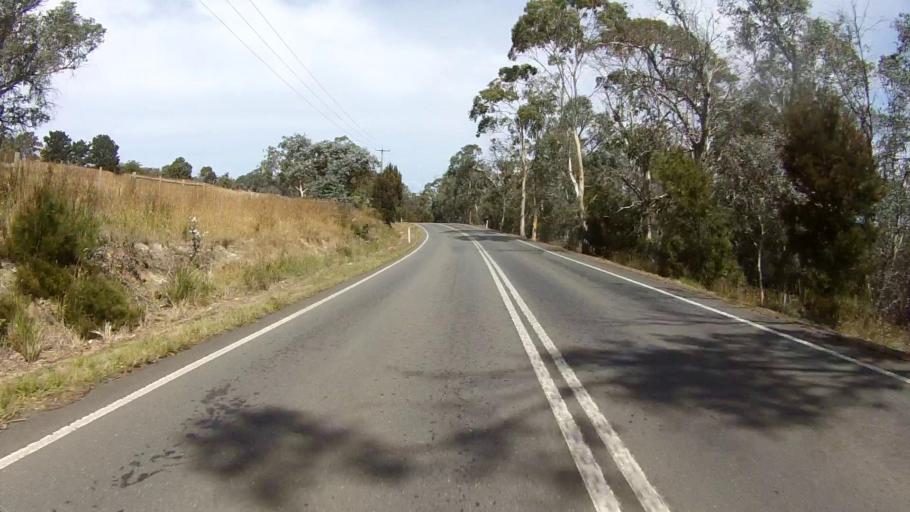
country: AU
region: Tasmania
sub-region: Clarence
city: Sandford
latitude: -42.9779
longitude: 147.5023
